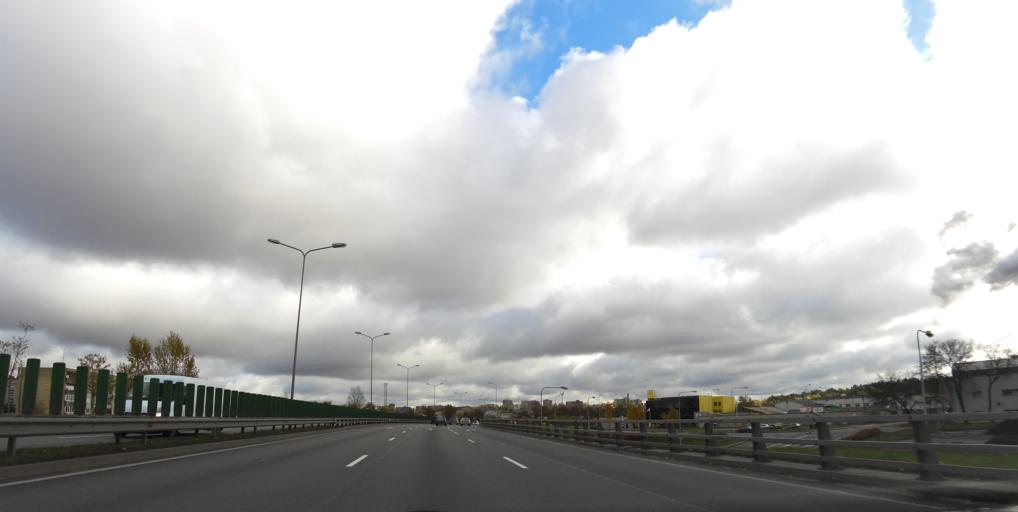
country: LT
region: Vilnius County
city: Vilkpede
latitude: 54.6665
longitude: 25.2495
